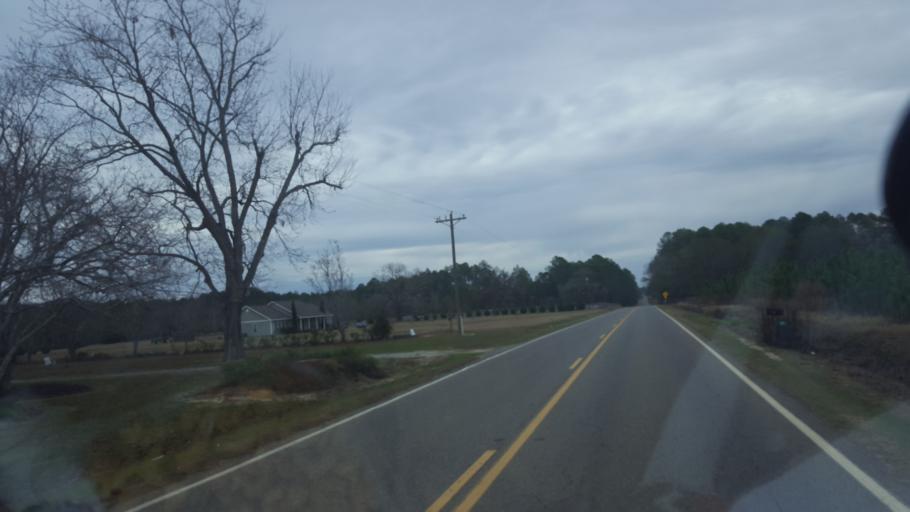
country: US
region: Georgia
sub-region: Ben Hill County
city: Fitzgerald
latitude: 31.7436
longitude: -83.2760
